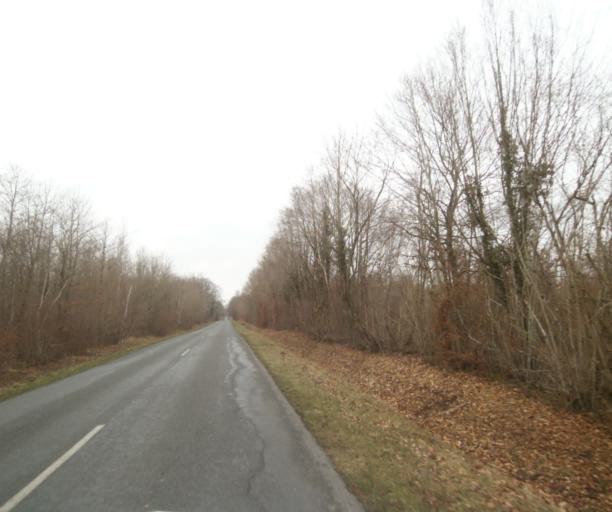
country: FR
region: Champagne-Ardenne
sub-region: Departement de la Marne
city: Pargny-sur-Saulx
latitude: 48.7237
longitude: 4.8729
